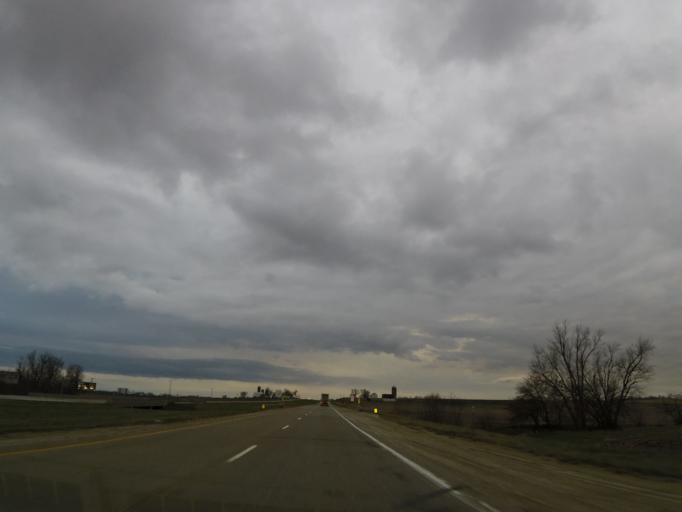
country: US
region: Iowa
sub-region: Henry County
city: Mount Pleasant
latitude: 40.7841
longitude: -91.5646
